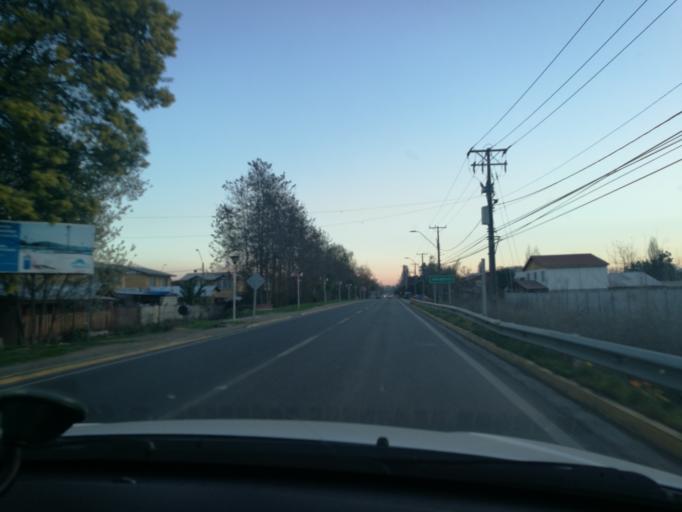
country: CL
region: O'Higgins
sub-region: Provincia de Cachapoal
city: Graneros
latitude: -34.0573
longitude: -70.7279
